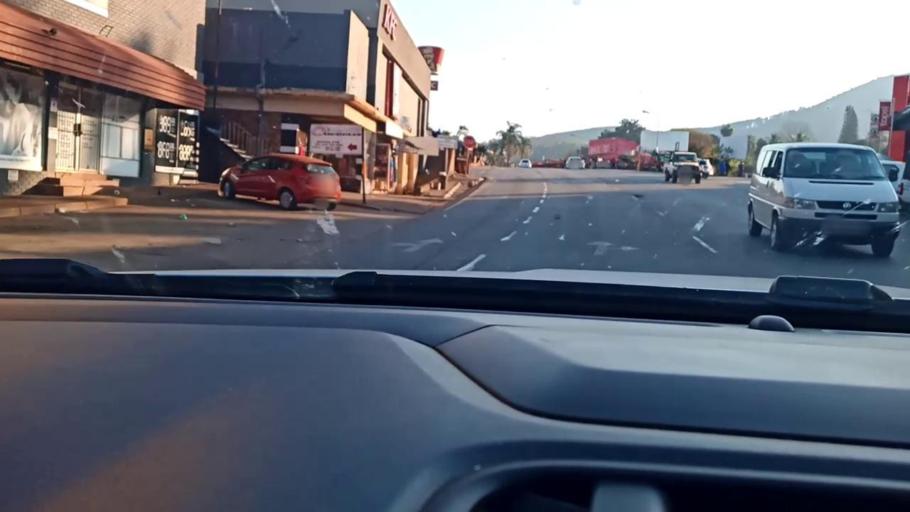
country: ZA
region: Limpopo
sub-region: Mopani District Municipality
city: Duiwelskloof
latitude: -23.6955
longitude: 30.1421
